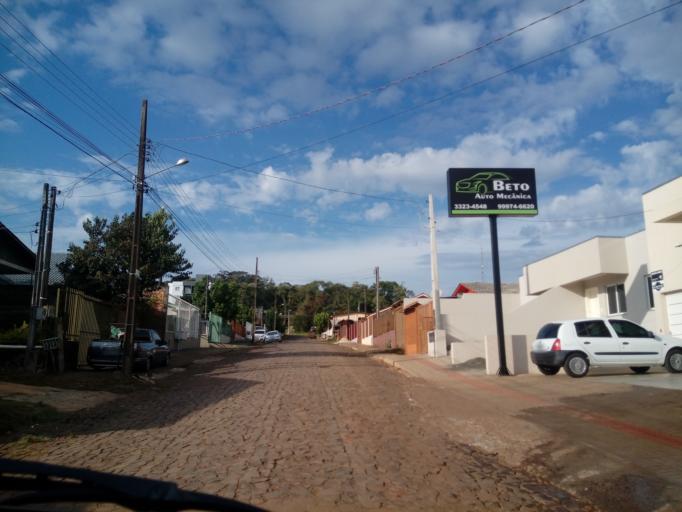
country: BR
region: Santa Catarina
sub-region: Chapeco
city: Chapeco
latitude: -27.0857
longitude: -52.5972
